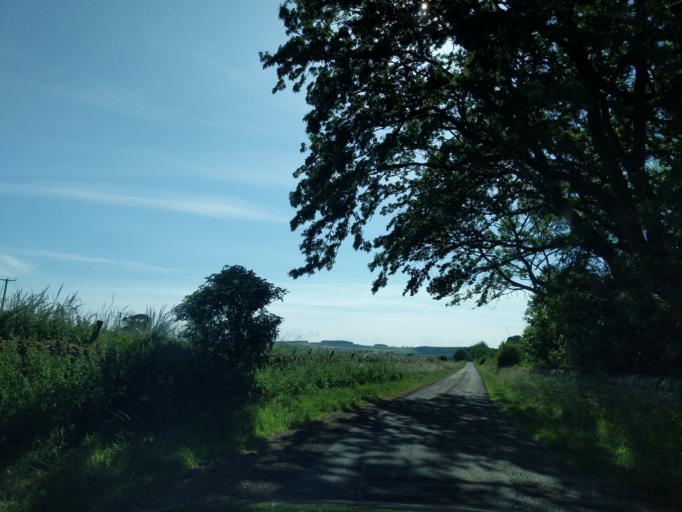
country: GB
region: Scotland
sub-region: Fife
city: Pathhead
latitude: 55.8774
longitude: -2.9510
